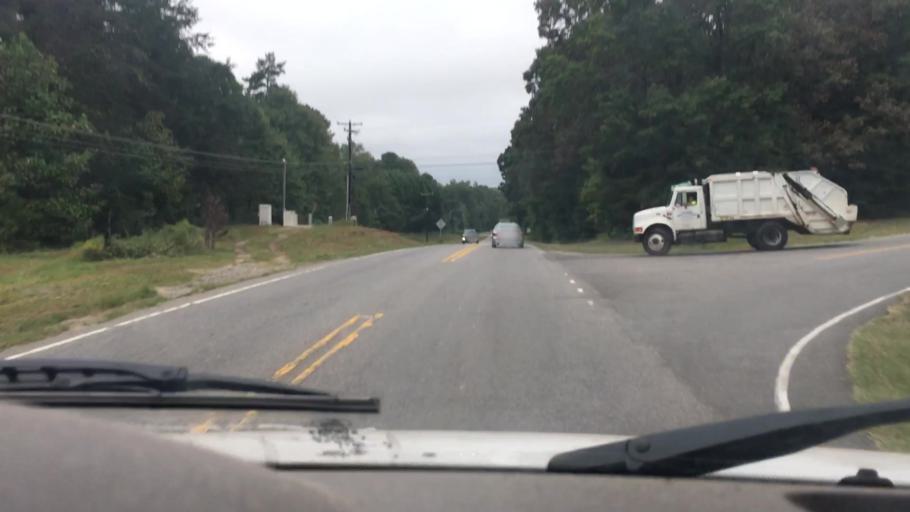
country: US
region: North Carolina
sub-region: Catawba County
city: Lake Norman of Catawba
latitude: 35.6018
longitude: -80.9199
